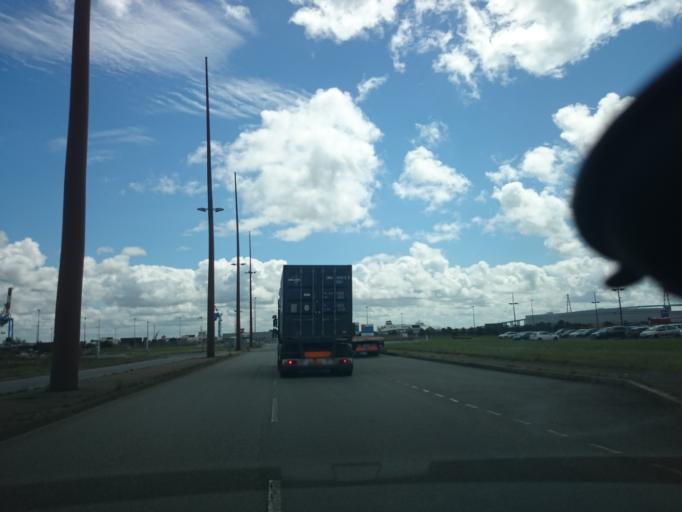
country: FR
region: Pays de la Loire
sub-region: Departement de la Loire-Atlantique
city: Trignac
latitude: 47.3020
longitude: -2.1648
